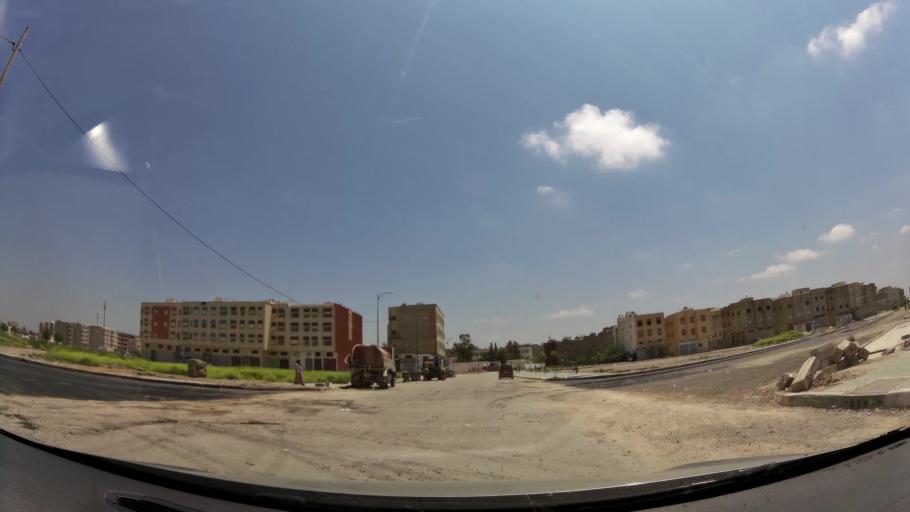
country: MA
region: Fes-Boulemane
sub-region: Fes
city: Fes
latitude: 34.0339
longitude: -5.0479
